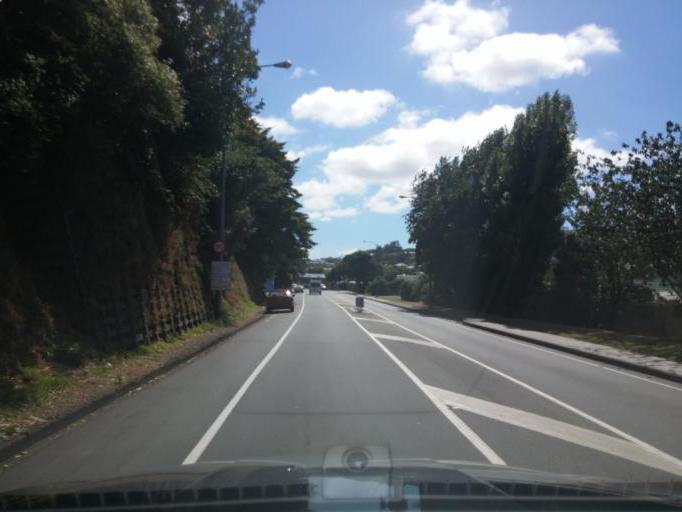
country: NZ
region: Wellington
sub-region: Porirua City
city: Porirua
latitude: -41.1804
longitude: 174.8244
